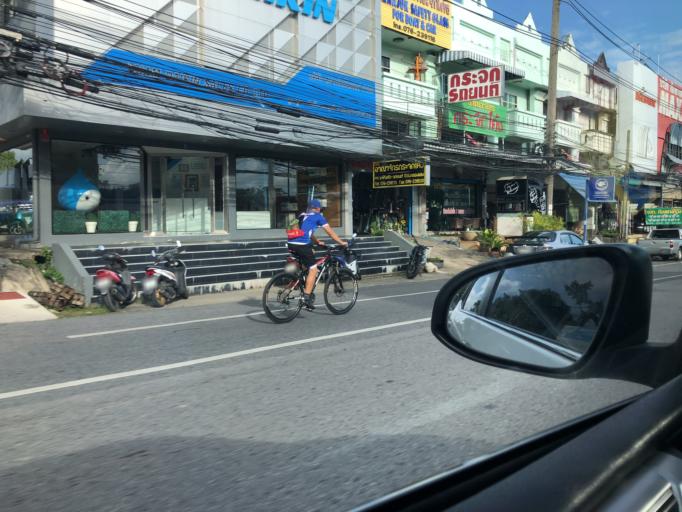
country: TH
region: Phuket
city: Ban Ko Kaeo
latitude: 7.9249
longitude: 98.3960
